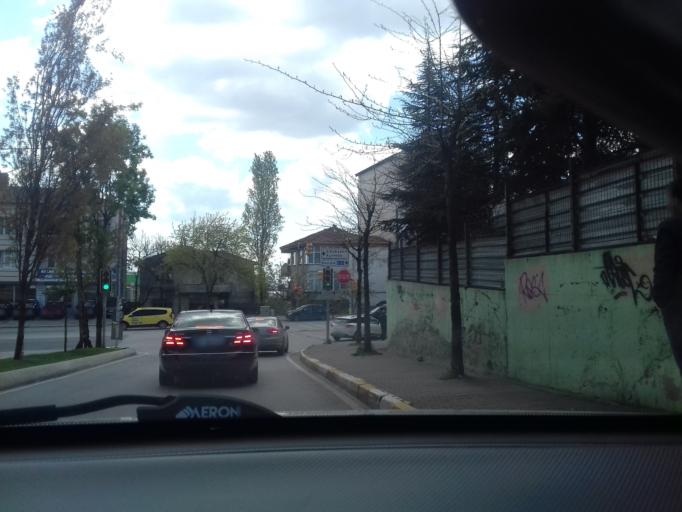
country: TR
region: Istanbul
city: Pendik
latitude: 40.9051
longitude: 29.2793
